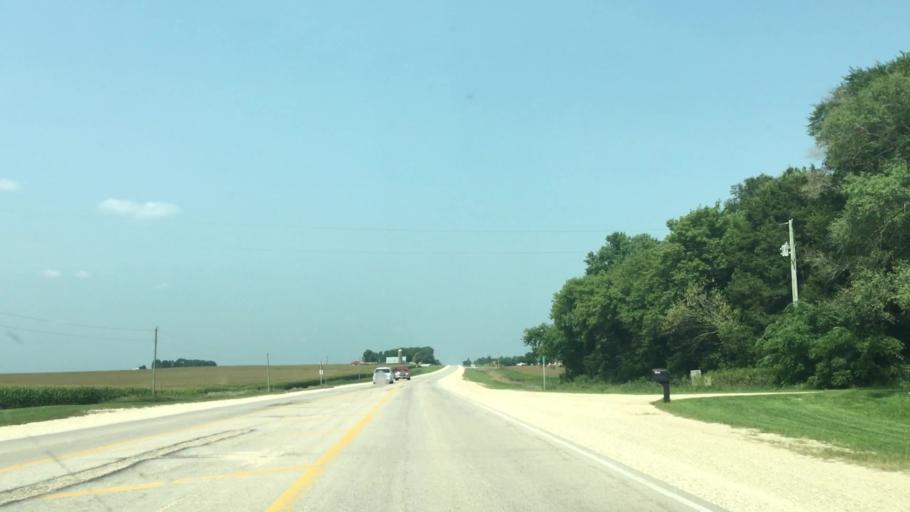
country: US
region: Iowa
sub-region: Fayette County
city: Fayette
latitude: 42.7616
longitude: -91.8044
